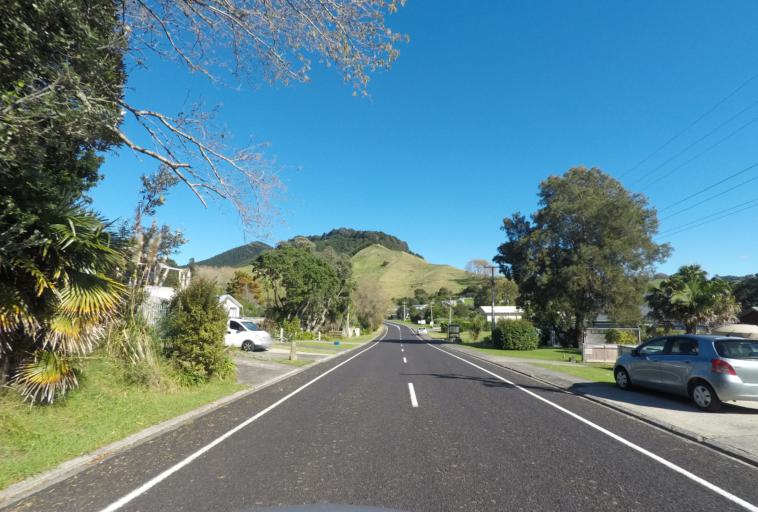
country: NZ
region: Waikato
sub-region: Thames-Coromandel District
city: Whangamata
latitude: -37.2836
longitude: 175.8988
